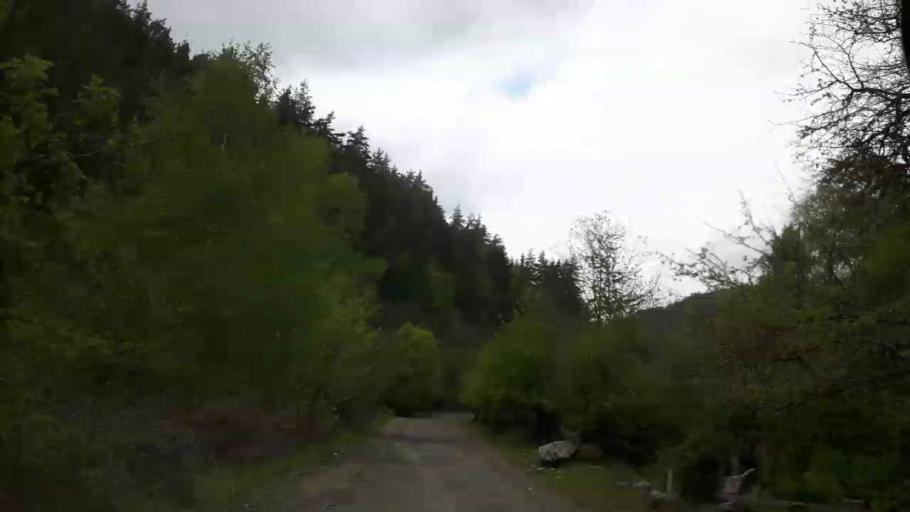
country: GE
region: Shida Kartli
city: Gori
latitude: 41.8607
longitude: 43.9557
